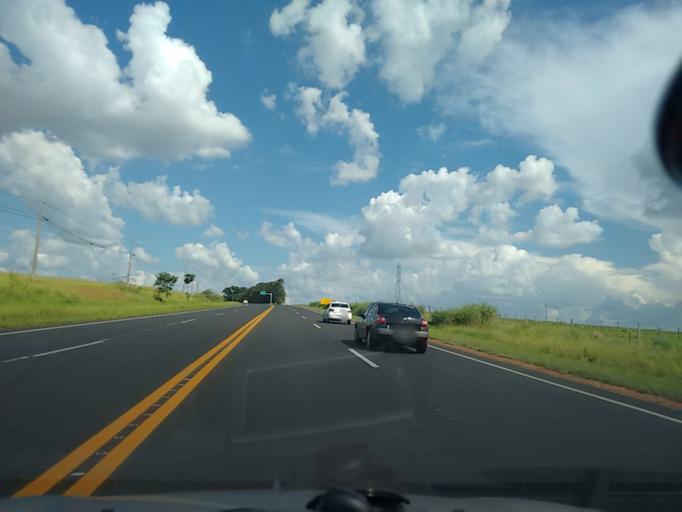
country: BR
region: Sao Paulo
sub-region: Marilia
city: Marilia
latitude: -22.1739
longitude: -49.9807
